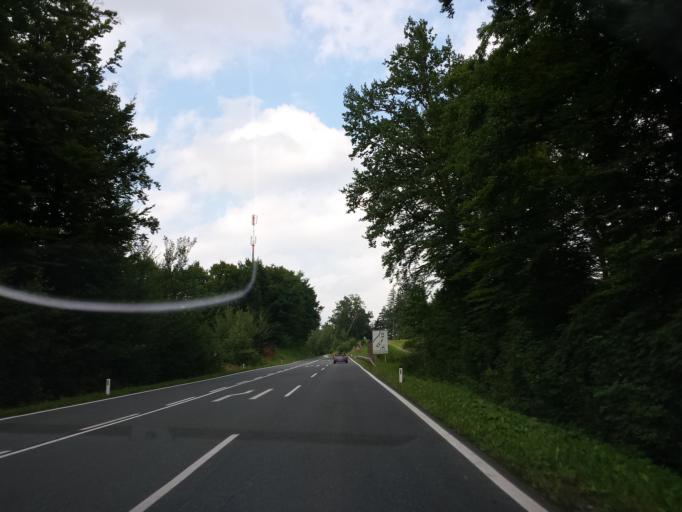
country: AT
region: Styria
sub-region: Politischer Bezirk Deutschlandsberg
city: Rassach
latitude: 46.8487
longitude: 15.2723
